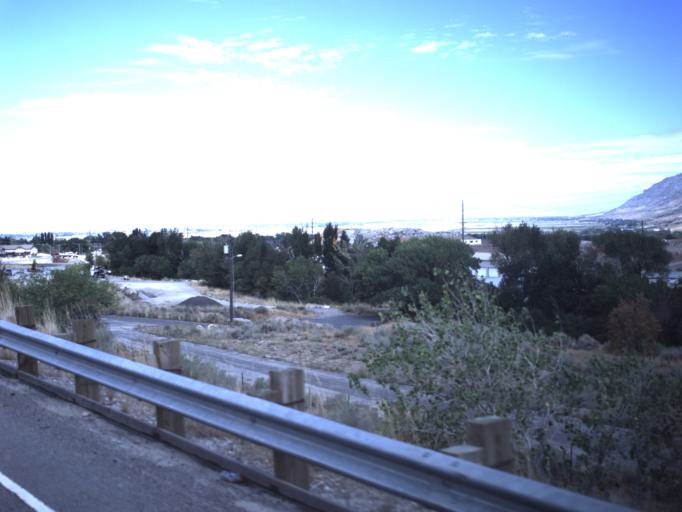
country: US
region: Utah
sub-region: Box Elder County
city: Brigham City
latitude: 41.5000
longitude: -111.9933
